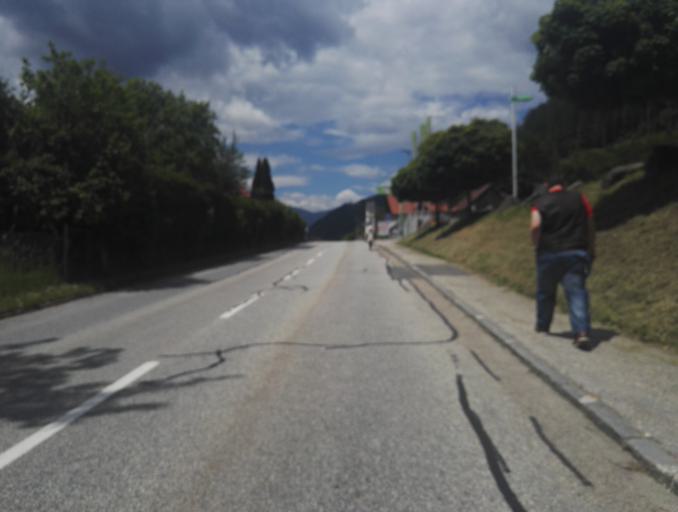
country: AT
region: Styria
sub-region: Politischer Bezirk Graz-Umgebung
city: Ubelbach
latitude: 47.2233
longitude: 15.2434
